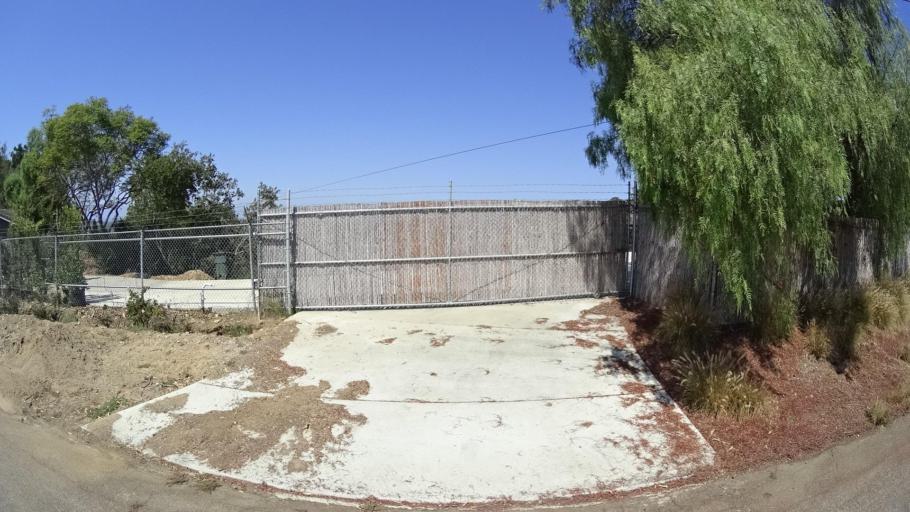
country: US
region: California
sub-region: San Diego County
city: San Marcos
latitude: 33.1734
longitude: -117.1908
